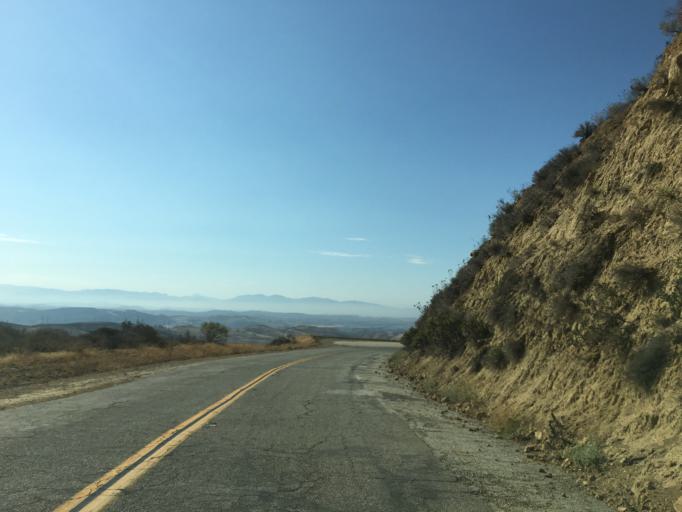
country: US
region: California
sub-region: Los Angeles County
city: Castaic
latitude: 34.5513
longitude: -118.6549
